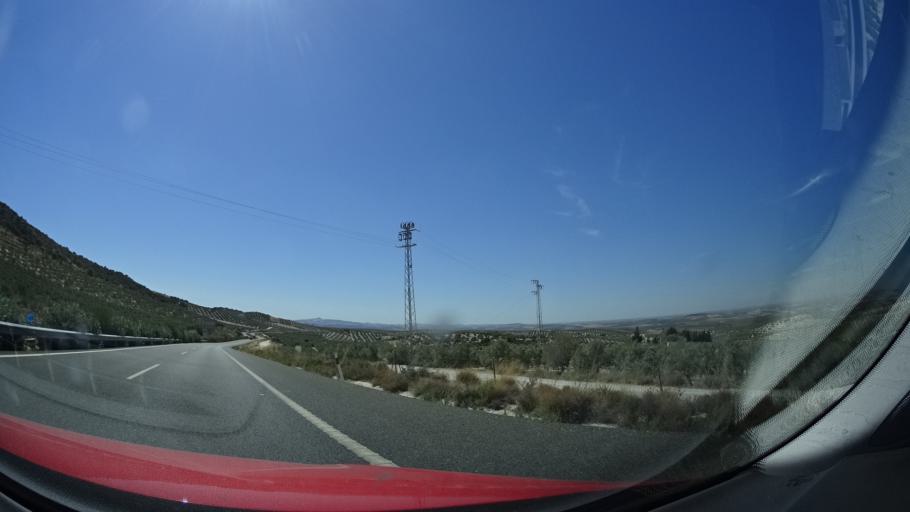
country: ES
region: Andalusia
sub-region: Provincia de Sevilla
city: Estepa
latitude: 37.2907
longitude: -4.9081
